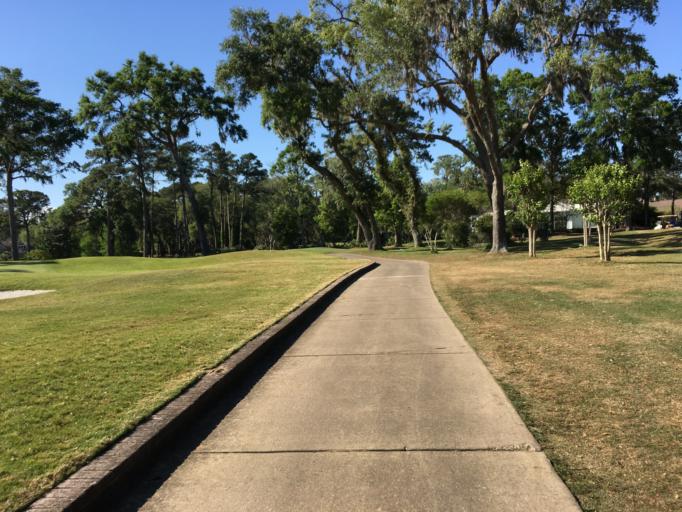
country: US
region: South Carolina
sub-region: Beaufort County
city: Hilton Head Island
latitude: 32.1993
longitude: -80.7453
